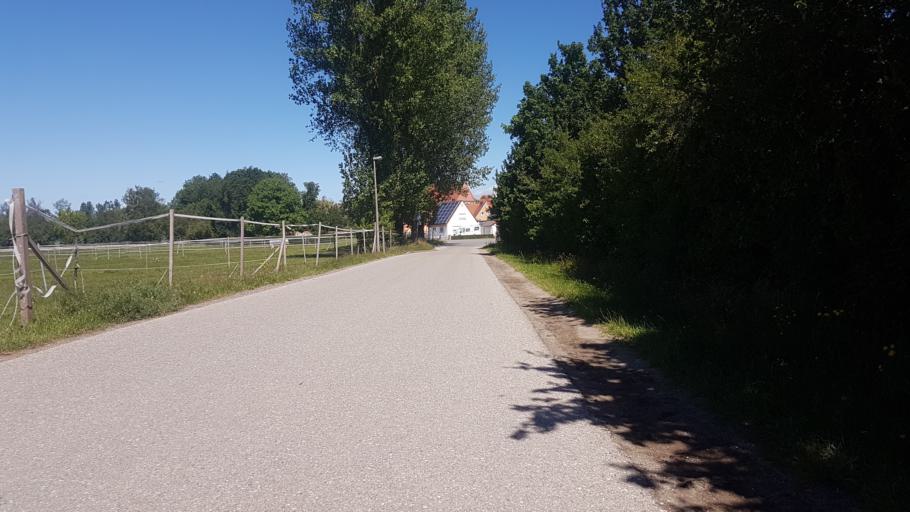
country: DE
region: Bavaria
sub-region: Regierungsbezirk Mittelfranken
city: Herrieden
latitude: 49.2293
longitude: 10.5014
